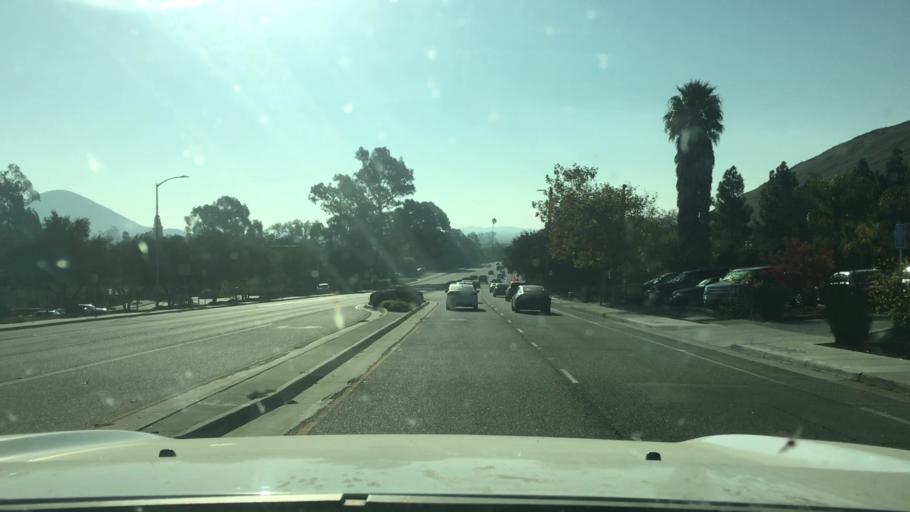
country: US
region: California
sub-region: San Luis Obispo County
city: San Luis Obispo
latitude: 35.2610
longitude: -120.6498
